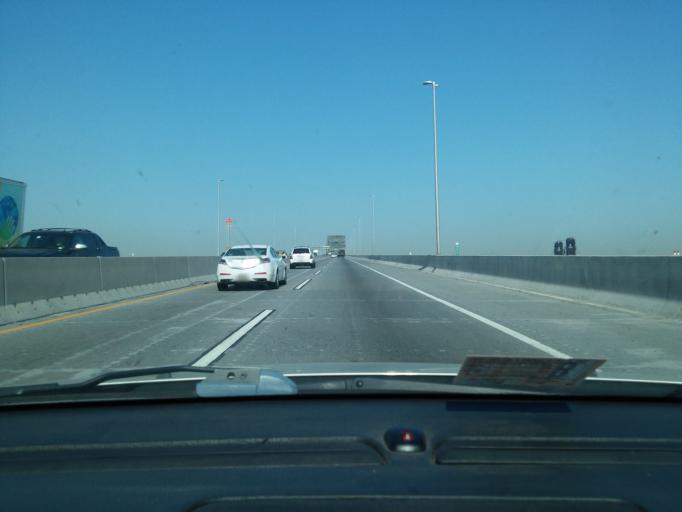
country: US
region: New Jersey
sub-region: Hudson County
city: Bayonne
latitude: 40.6930
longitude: -74.1107
